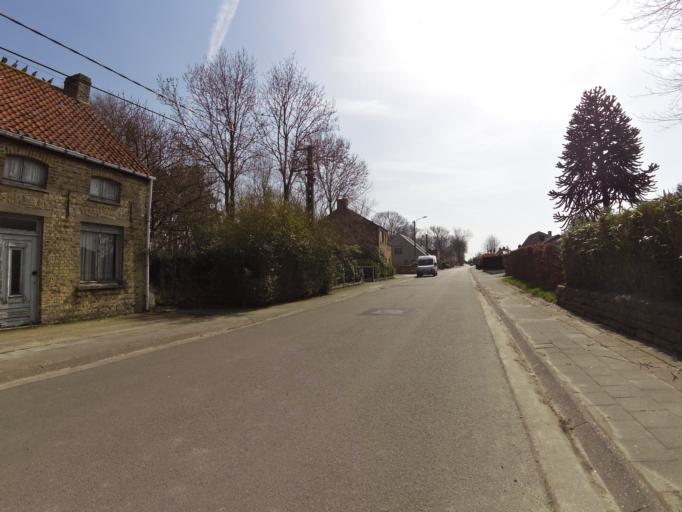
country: BE
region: Flanders
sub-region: Provincie West-Vlaanderen
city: Gistel
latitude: 51.1277
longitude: 2.9673
